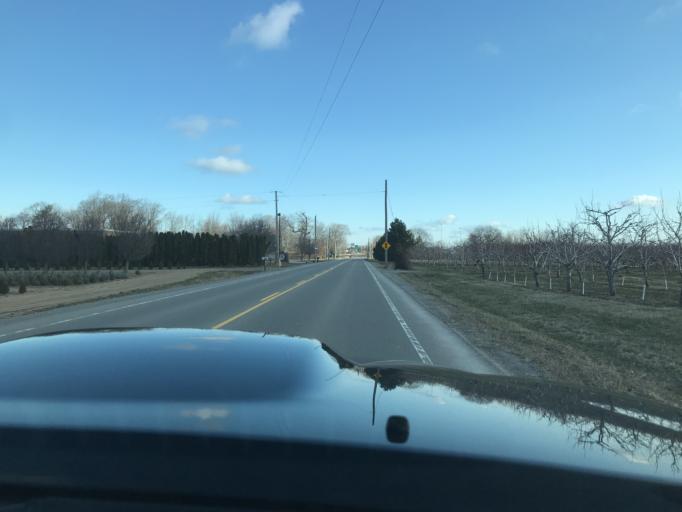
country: CA
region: Ontario
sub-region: Regional Municipality of Niagara
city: St. Catharines
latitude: 43.1737
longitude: -79.3086
